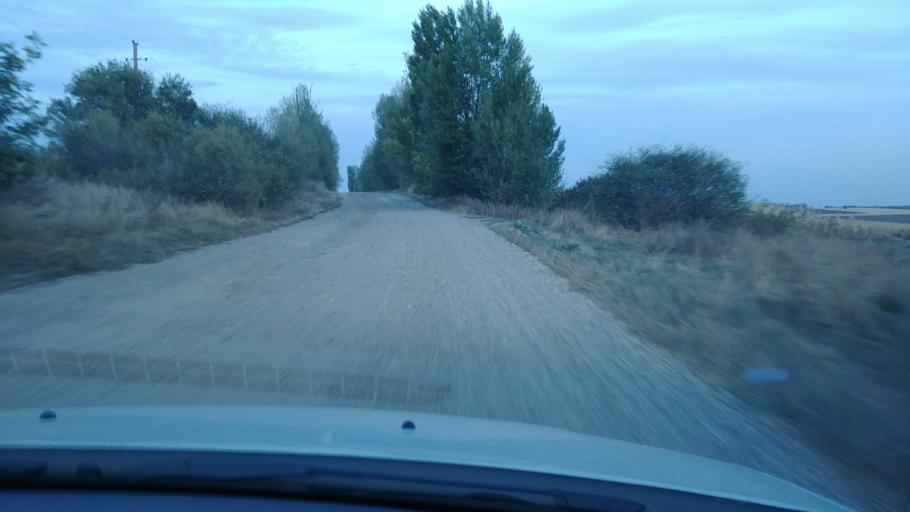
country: MD
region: Rezina
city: Saharna
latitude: 47.6767
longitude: 28.9272
